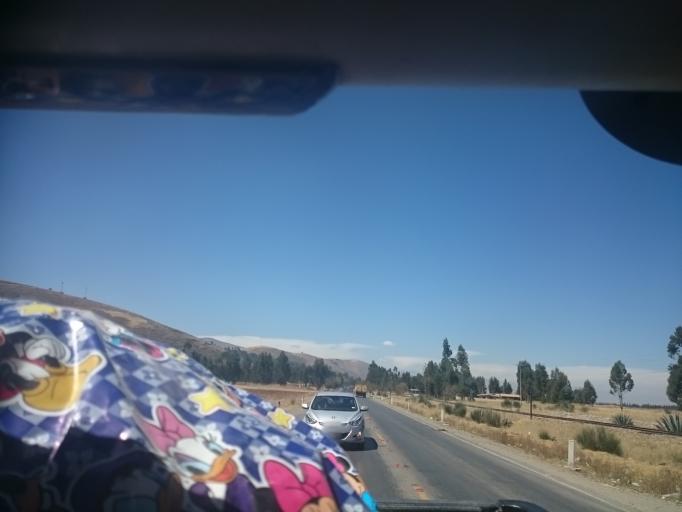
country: PE
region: Junin
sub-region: Provincia de Jauja
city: Huaripampa
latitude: -11.7929
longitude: -75.4610
